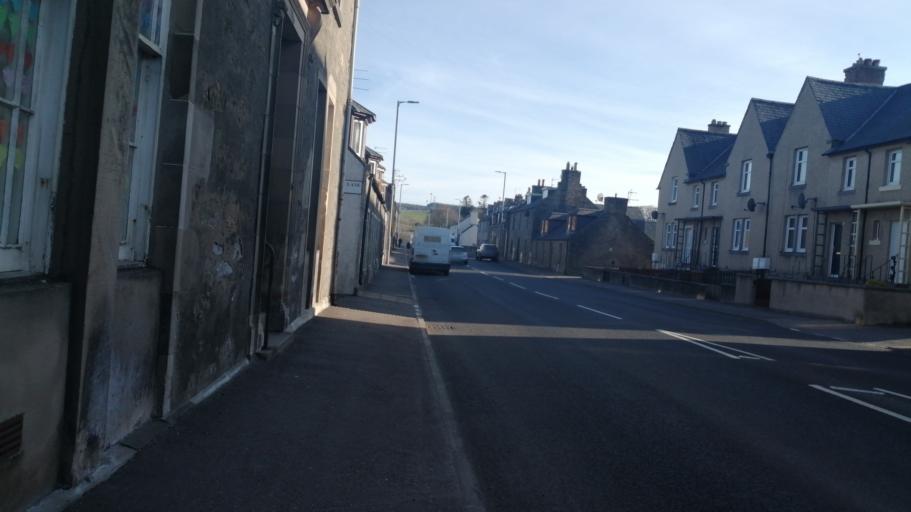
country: GB
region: Scotland
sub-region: Moray
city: Keith
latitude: 57.5380
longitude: -2.9487
